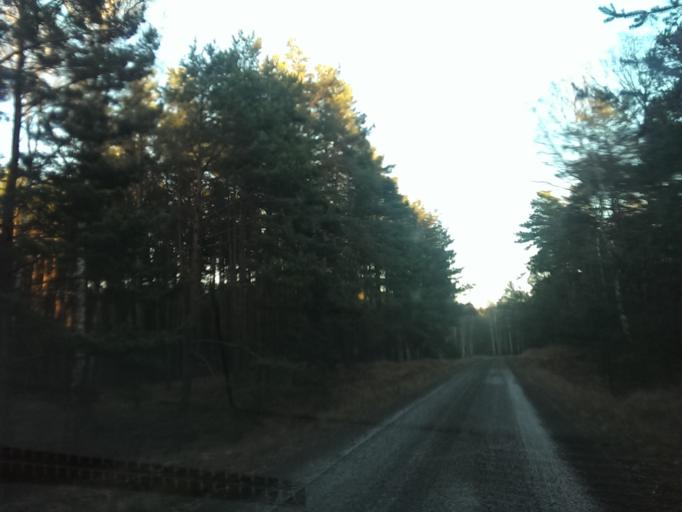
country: PL
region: Kujawsko-Pomorskie
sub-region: Powiat nakielski
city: Naklo nad Notecia
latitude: 53.0504
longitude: 17.6147
